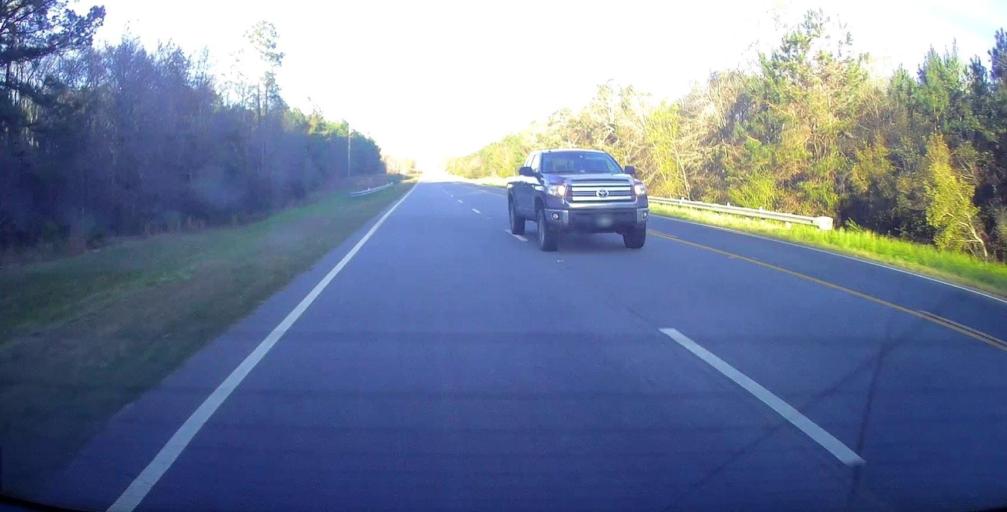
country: US
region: Georgia
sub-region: Wilcox County
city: Rochelle
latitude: 31.9645
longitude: -83.3912
